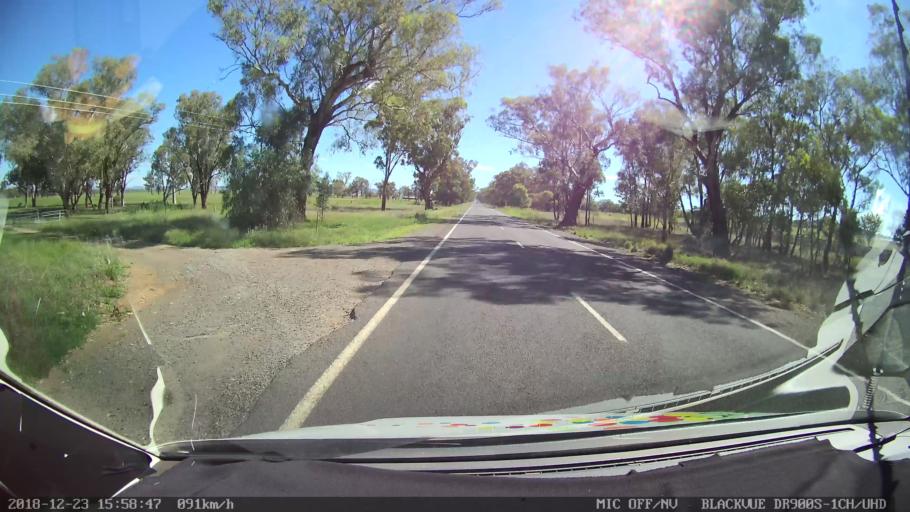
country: AU
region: New South Wales
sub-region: Tamworth Municipality
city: Phillip
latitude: -31.1922
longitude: 150.8388
